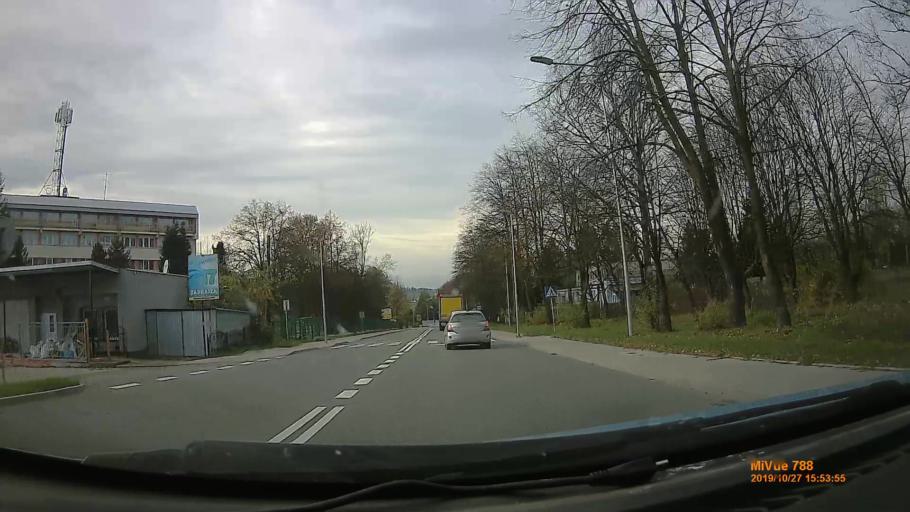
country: PL
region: Lower Silesian Voivodeship
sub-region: Powiat klodzki
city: Bozkow
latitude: 50.5399
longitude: 16.5624
